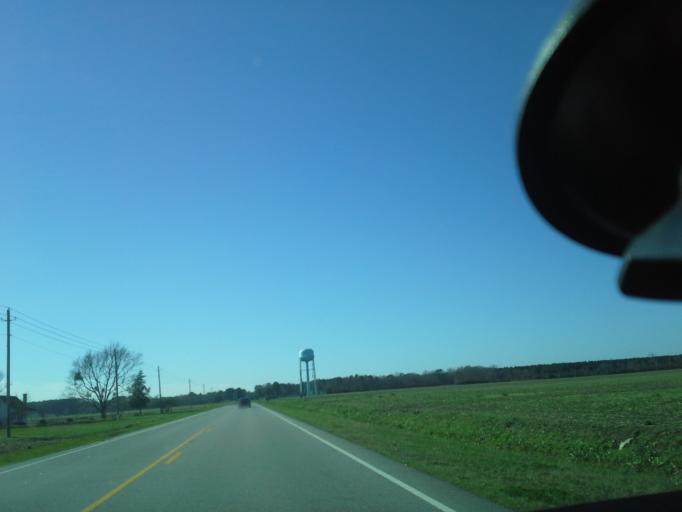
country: US
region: North Carolina
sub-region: Beaufort County
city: Belhaven
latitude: 35.5265
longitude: -76.7915
